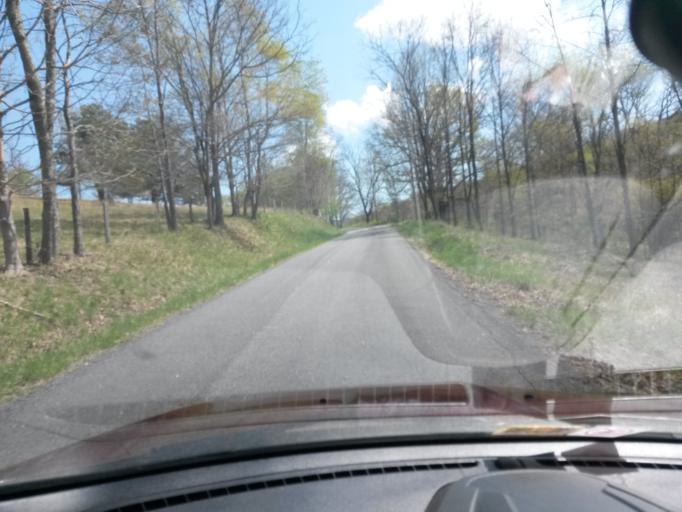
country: US
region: Virginia
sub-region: Highland County
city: Monterey
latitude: 38.2244
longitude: -79.6650
